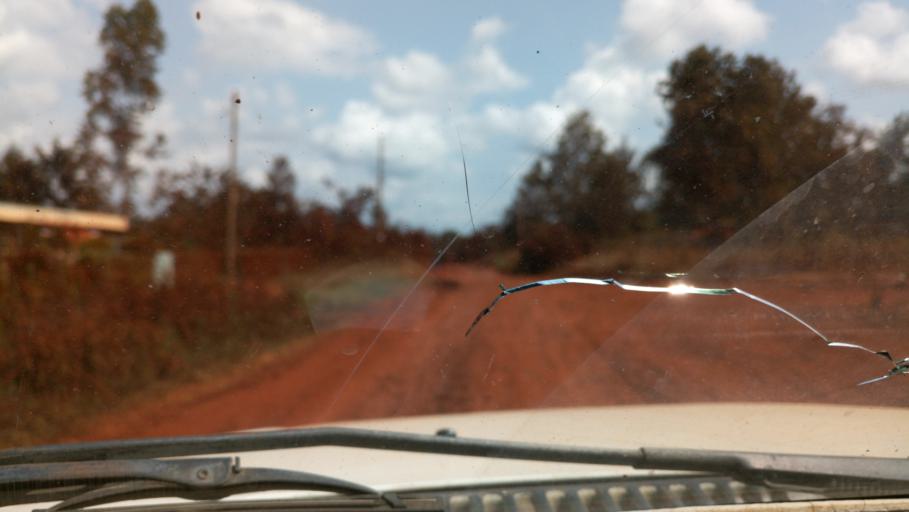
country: KE
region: Murang'a District
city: Karuri
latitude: -0.7473
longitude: 37.1983
